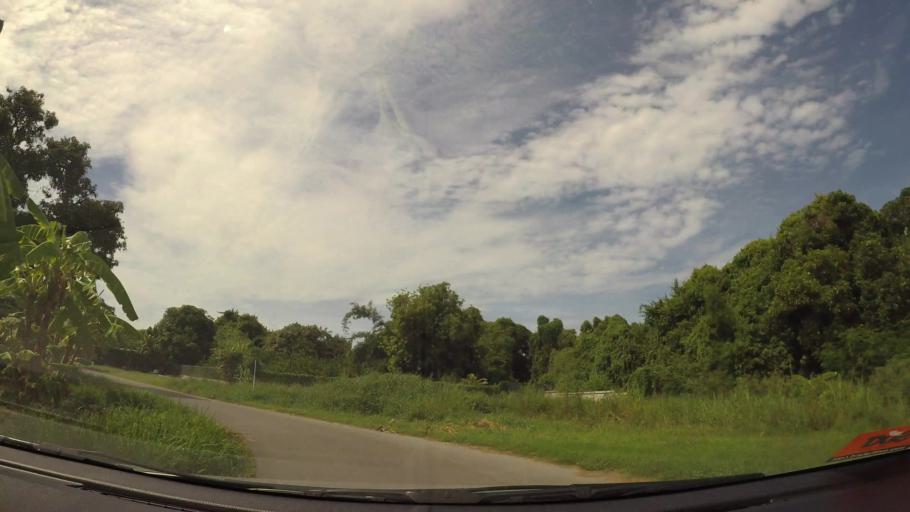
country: TH
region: Chon Buri
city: Sattahip
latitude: 12.6666
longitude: 100.9092
